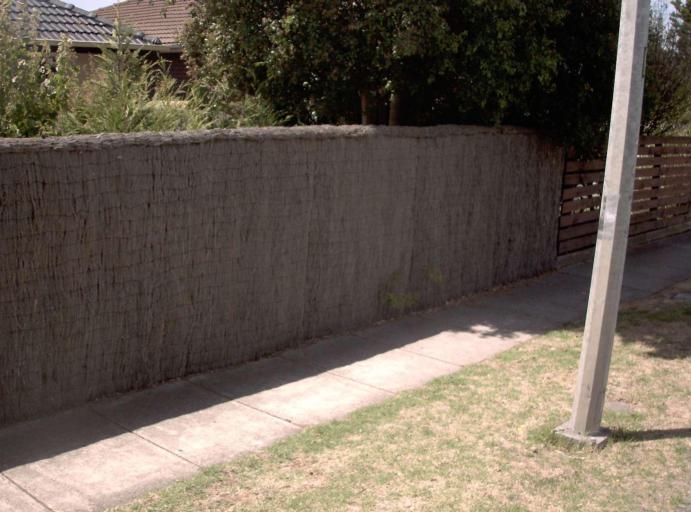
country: AU
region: Victoria
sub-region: Kingston
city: Mordialloc
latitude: -37.9846
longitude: 145.0934
